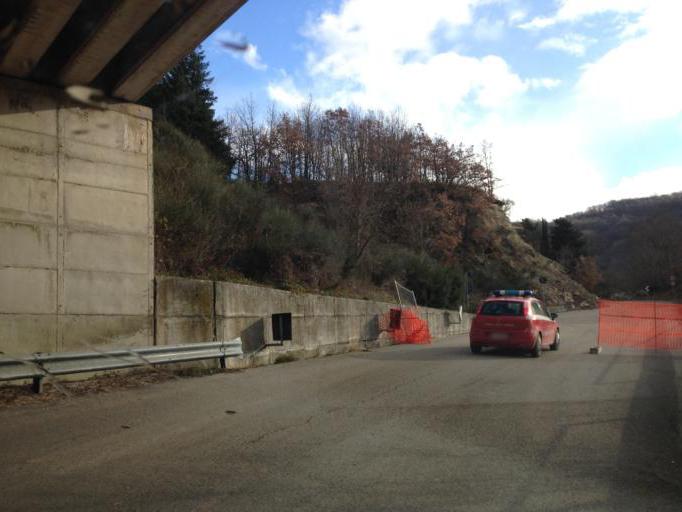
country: IT
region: The Marches
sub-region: Provincia di Ascoli Piceno
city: Arquata del Tronto
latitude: 42.7567
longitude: 13.2780
